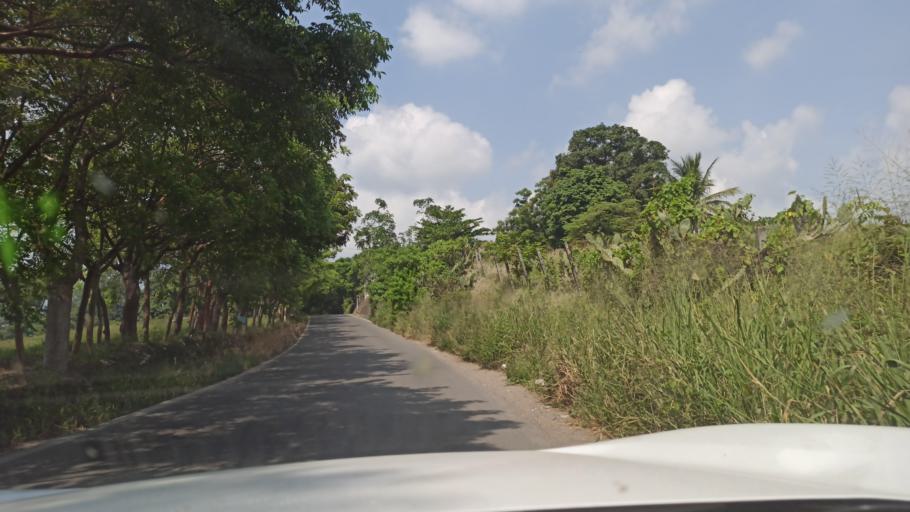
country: MX
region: Veracruz
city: Martinez de la Torre
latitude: 20.0815
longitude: -97.0698
